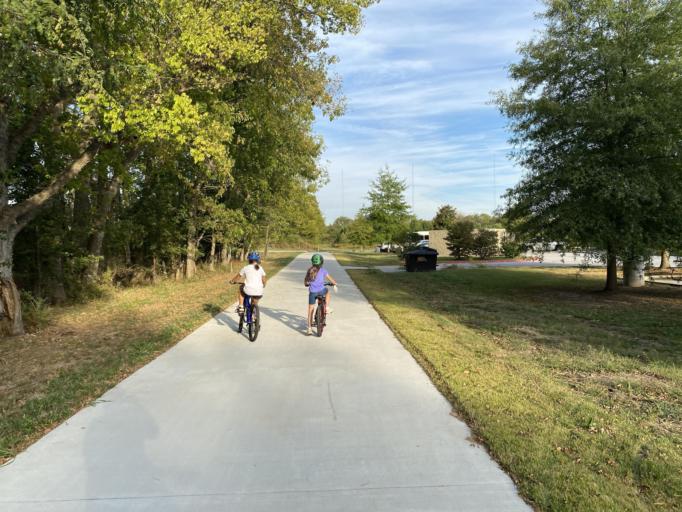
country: US
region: Arkansas
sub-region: Washington County
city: Johnson
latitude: 36.1102
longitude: -94.1873
